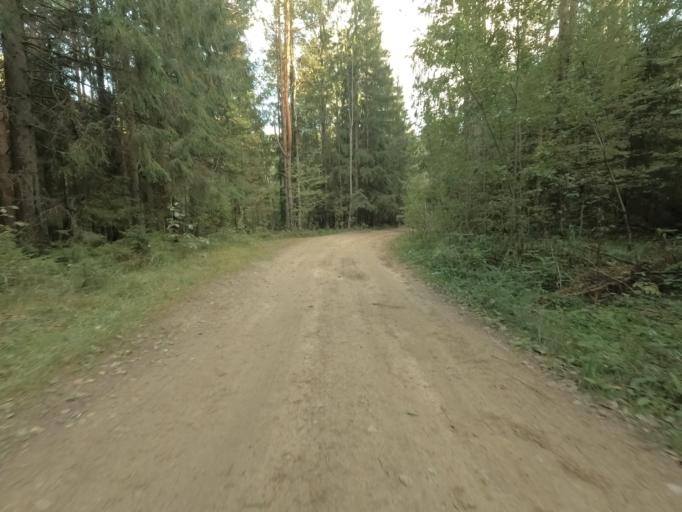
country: RU
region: Leningrad
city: Otradnoye
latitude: 59.8519
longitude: 30.7962
